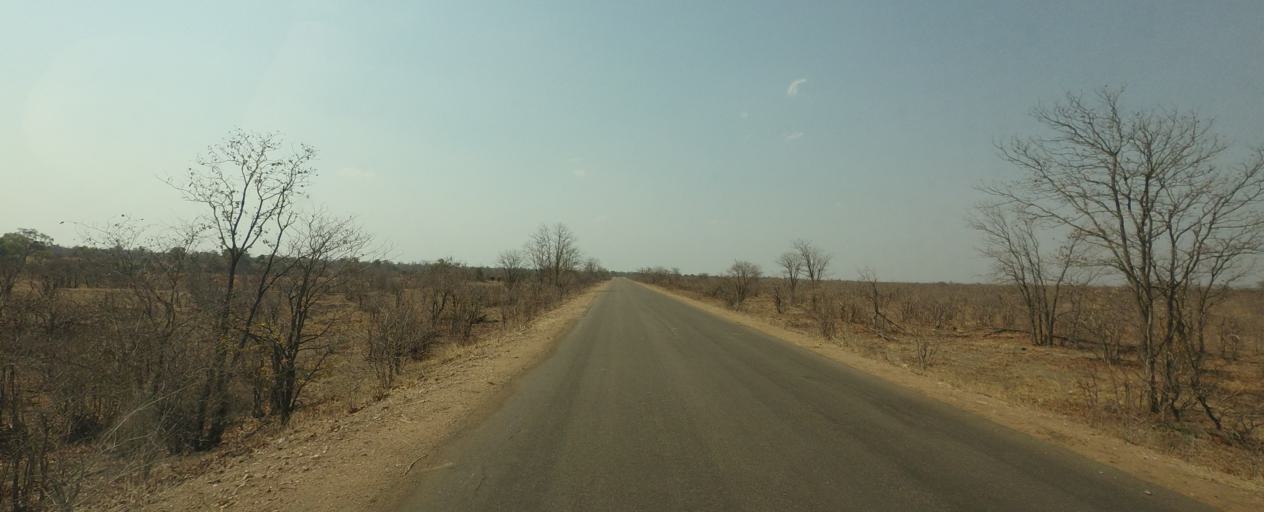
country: ZA
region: Limpopo
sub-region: Mopani District Municipality
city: Giyani
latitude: -23.1621
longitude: 31.3484
